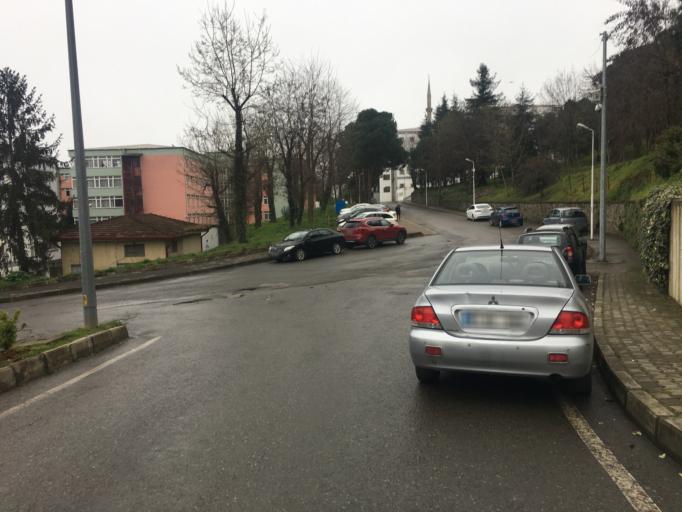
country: TR
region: Trabzon
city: Trabzon
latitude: 40.9949
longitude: 39.7675
